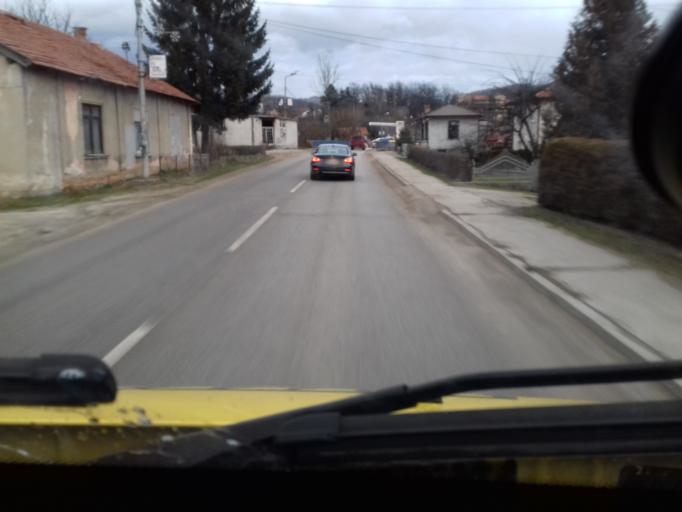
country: BA
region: Federation of Bosnia and Herzegovina
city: Vitez
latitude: 44.1483
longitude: 17.8036
